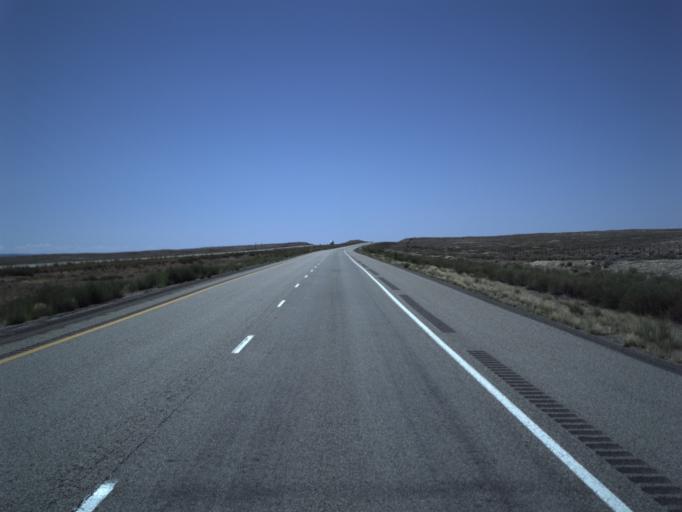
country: US
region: Utah
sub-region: Grand County
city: Moab
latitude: 39.0143
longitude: -109.3049
